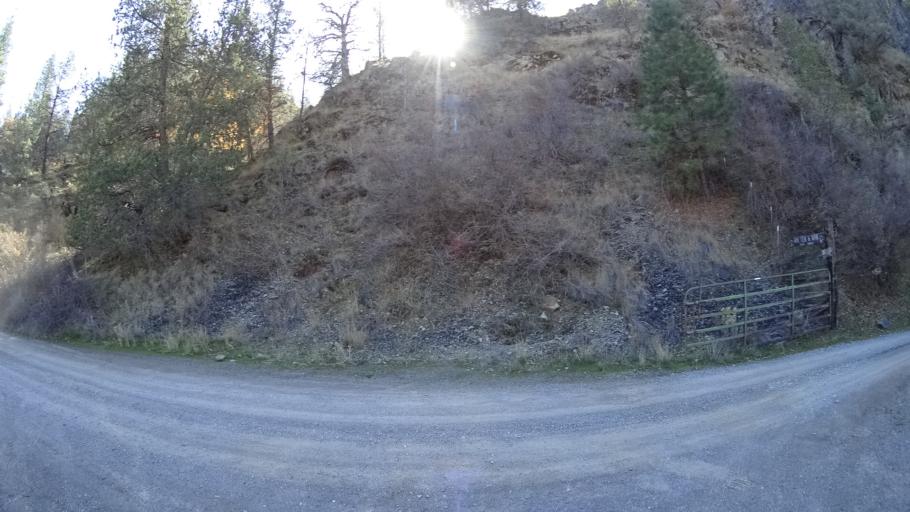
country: US
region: California
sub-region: Siskiyou County
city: Yreka
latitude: 41.8027
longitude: -122.6059
